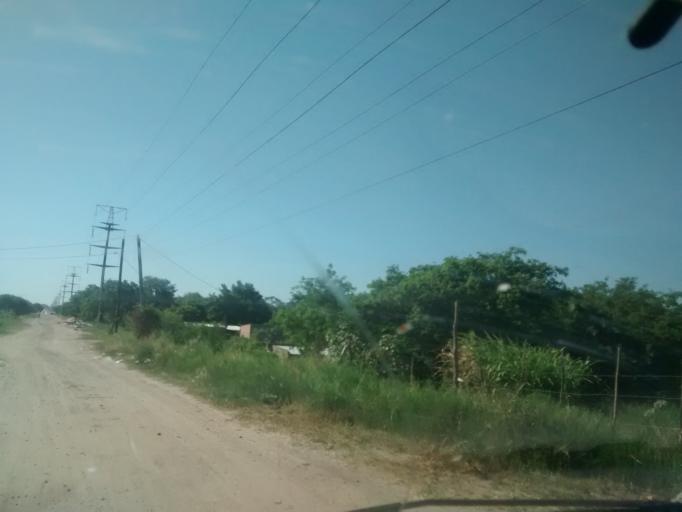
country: AR
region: Chaco
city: Resistencia
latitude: -27.4378
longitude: -58.9587
